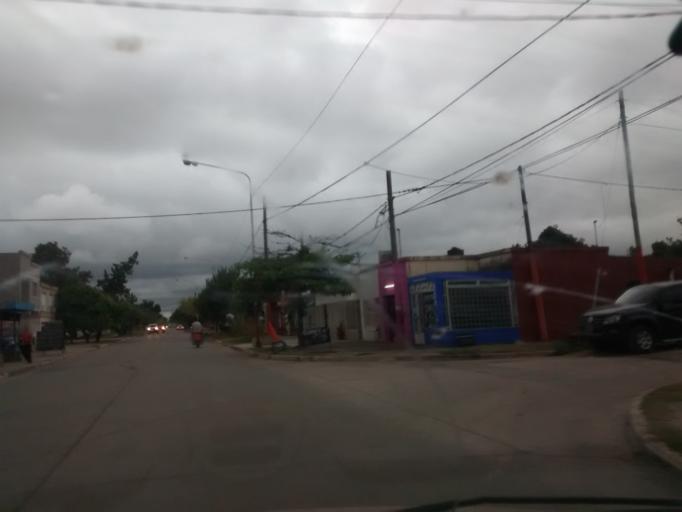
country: AR
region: Chaco
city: Resistencia
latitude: -27.4496
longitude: -59.0045
